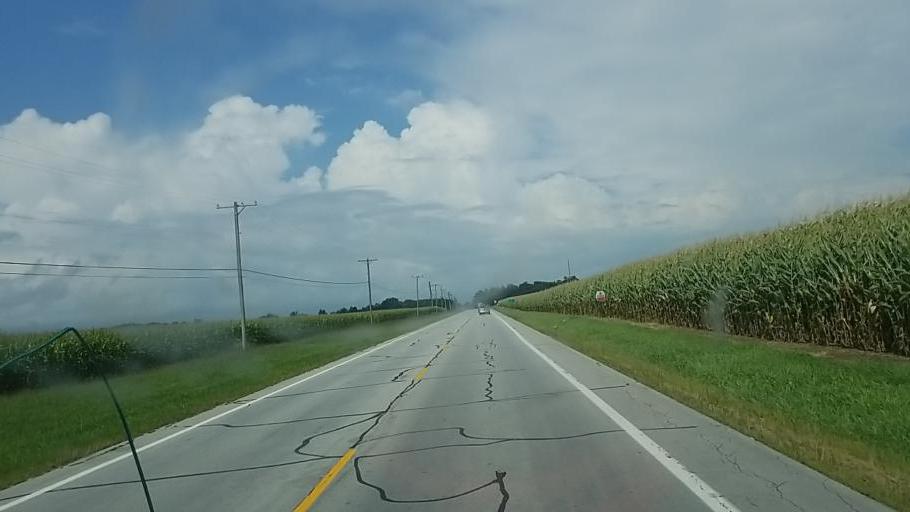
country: US
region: Ohio
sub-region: Champaign County
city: Urbana
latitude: 40.1373
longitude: -83.7474
